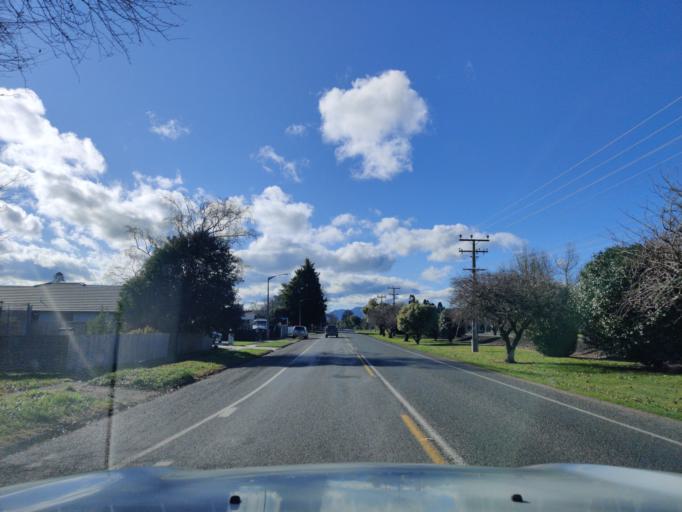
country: NZ
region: Waikato
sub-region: Matamata-Piako District
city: Matamata
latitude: -37.8271
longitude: 175.7691
